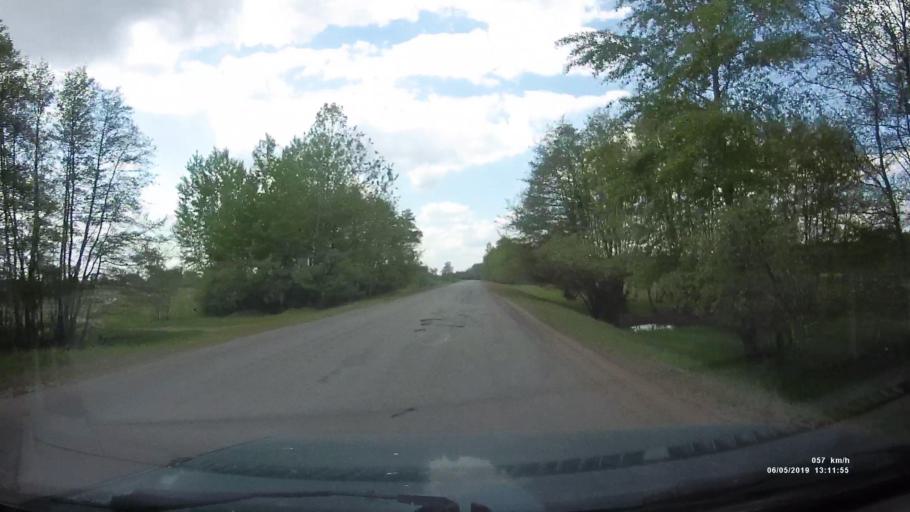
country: RU
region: Rostov
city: Ust'-Donetskiy
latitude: 47.7545
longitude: 40.9537
